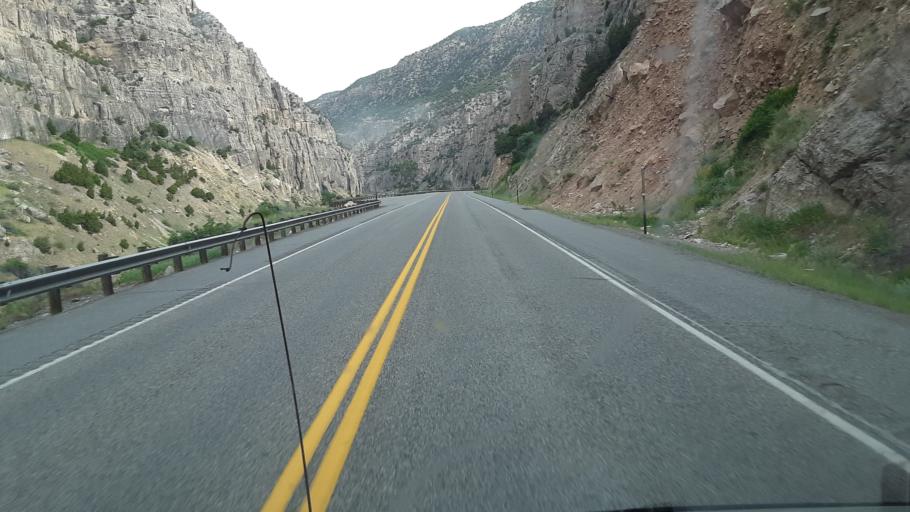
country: US
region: Wyoming
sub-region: Hot Springs County
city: Thermopolis
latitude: 43.5321
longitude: -108.1786
